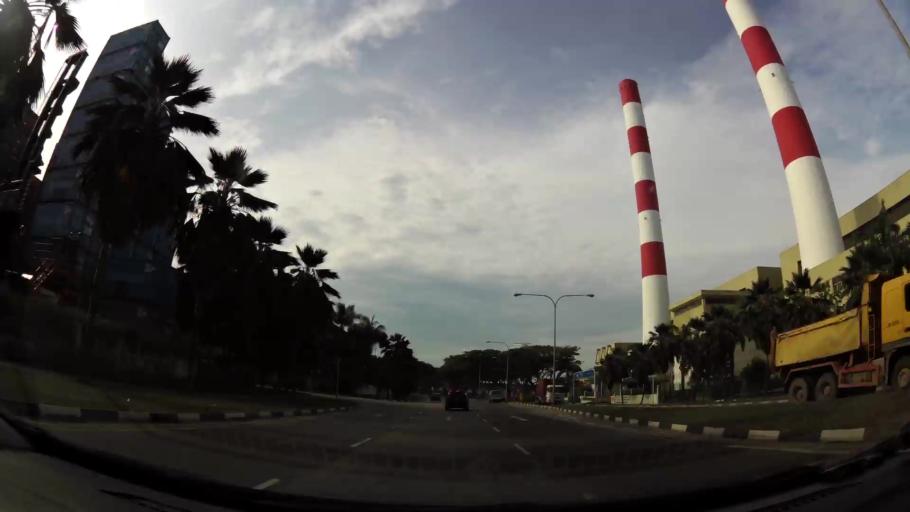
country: MY
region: Johor
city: Johor Bahru
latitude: 1.2967
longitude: 103.6223
